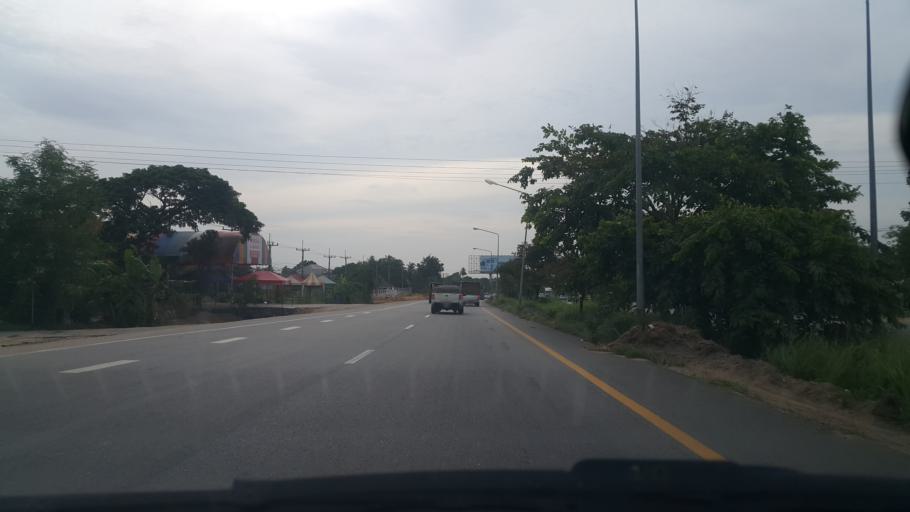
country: TH
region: Chon Buri
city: Bang Lamung
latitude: 12.9906
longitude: 100.9412
